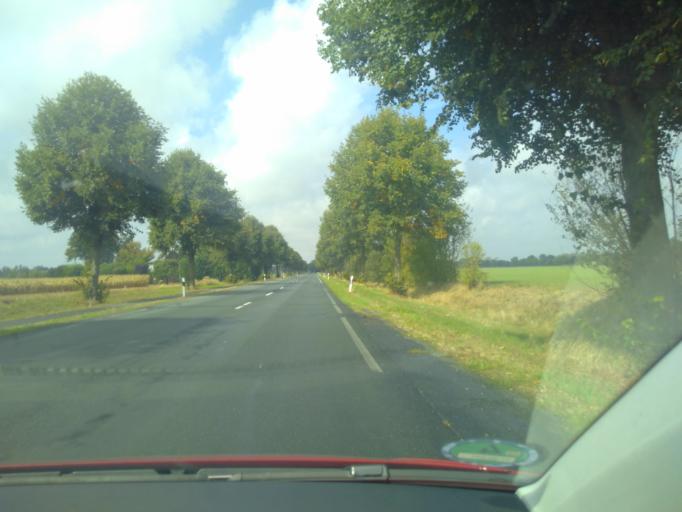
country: DE
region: North Rhine-Westphalia
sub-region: Regierungsbezirk Munster
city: Warendorf
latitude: 52.0013
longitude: 7.9358
